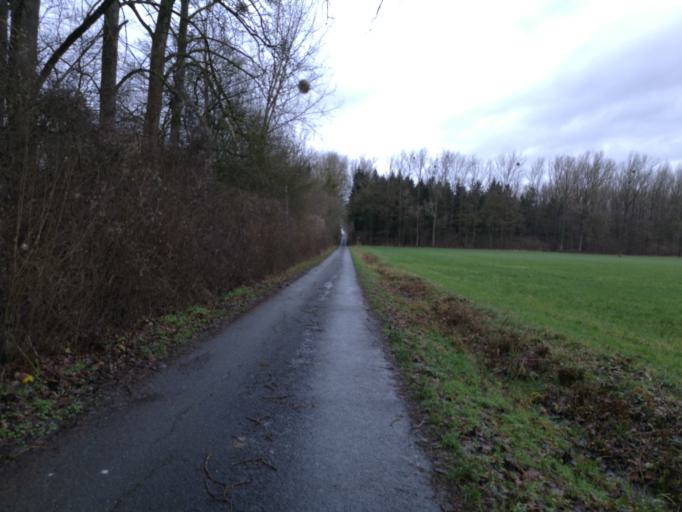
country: DE
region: North Rhine-Westphalia
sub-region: Regierungsbezirk Munster
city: Beckum
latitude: 51.6963
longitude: 8.1141
